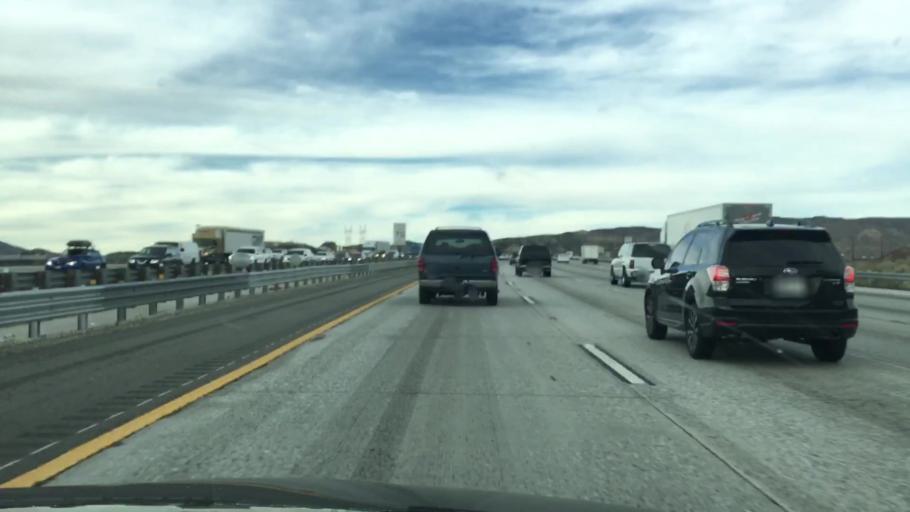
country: US
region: California
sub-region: San Bernardino County
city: Oak Hills
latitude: 34.3161
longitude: -117.4791
